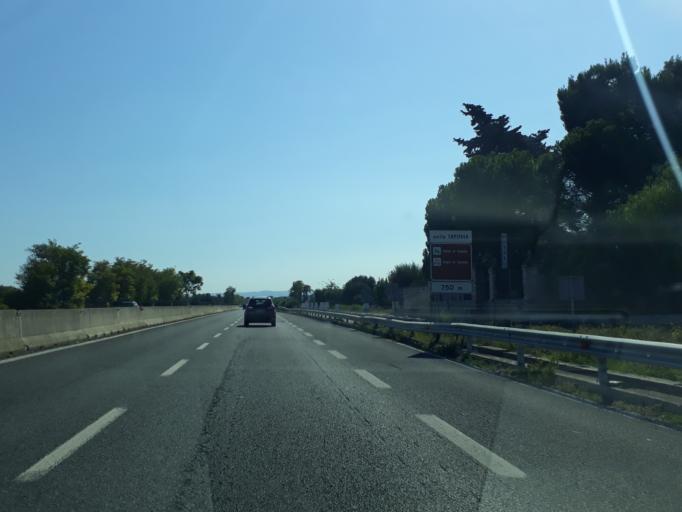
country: IT
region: Apulia
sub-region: Provincia di Bari
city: Monopoli
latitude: 40.9029
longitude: 17.3263
